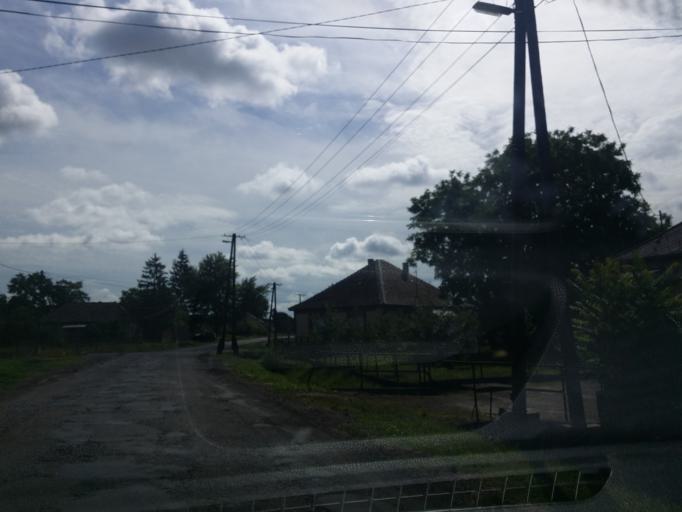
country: HU
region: Heves
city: Erdotelek
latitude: 47.6164
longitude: 20.3633
